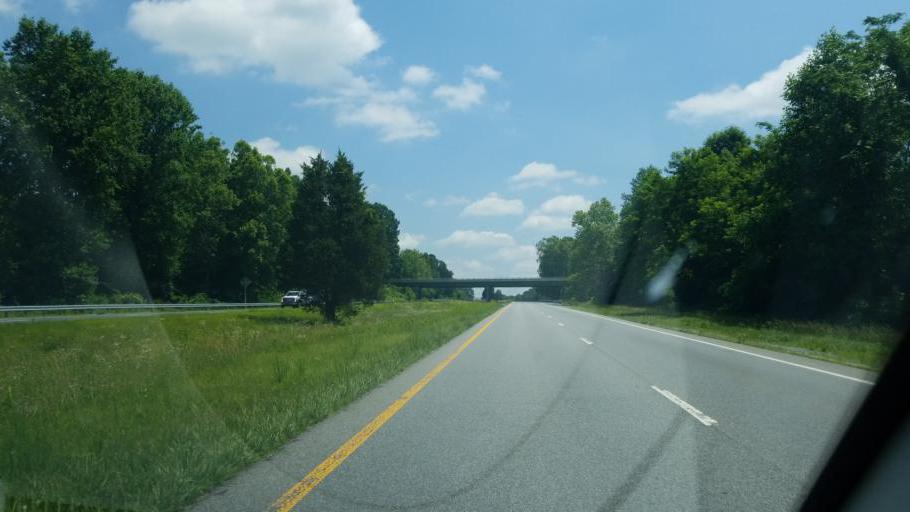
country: US
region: Virginia
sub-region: Campbell County
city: Altavista
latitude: 37.1269
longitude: -79.3098
